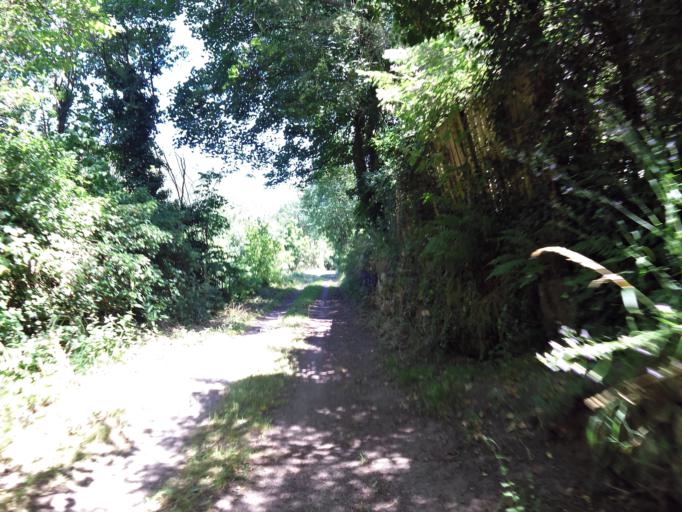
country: DE
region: Rheinland-Pfalz
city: Frankeneck
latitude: 49.3741
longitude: 8.0522
